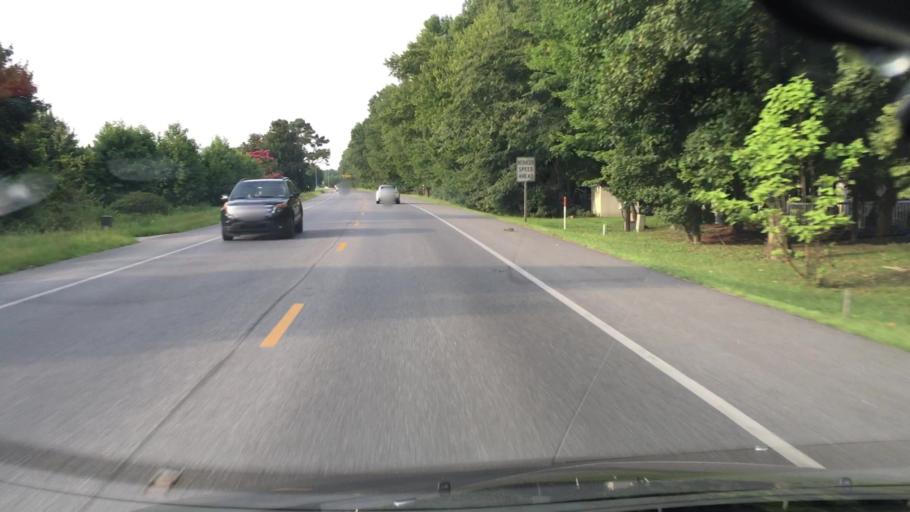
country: US
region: Maryland
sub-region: Worcester County
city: Ocean Pines
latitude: 38.3689
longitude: -75.1646
